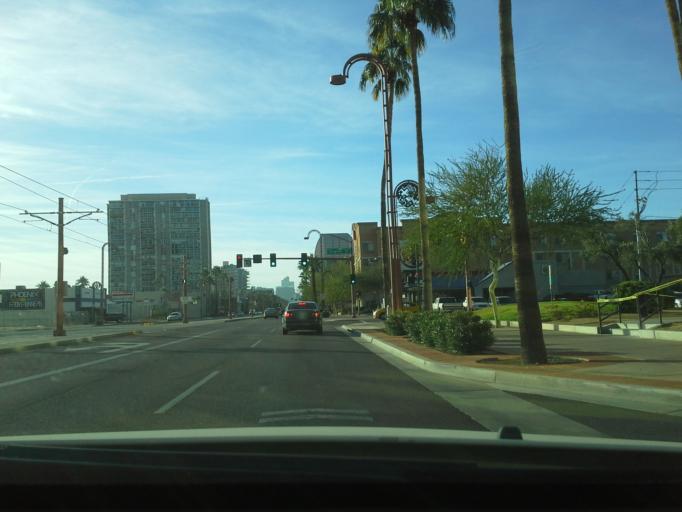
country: US
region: Arizona
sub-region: Maricopa County
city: Phoenix
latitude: 33.4771
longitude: -112.0740
